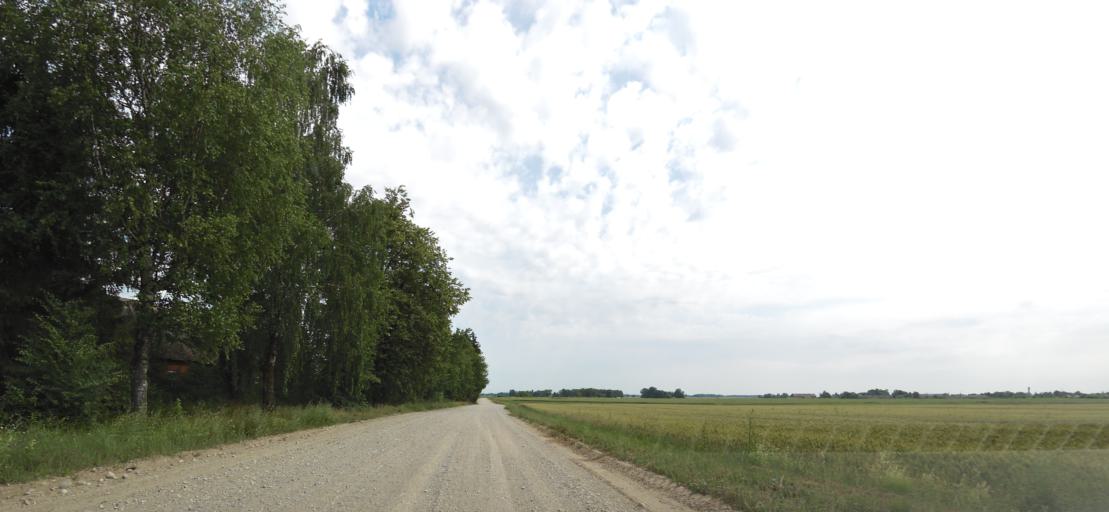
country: LT
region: Panevezys
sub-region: Birzai
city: Birzai
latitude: 56.2715
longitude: 24.5811
